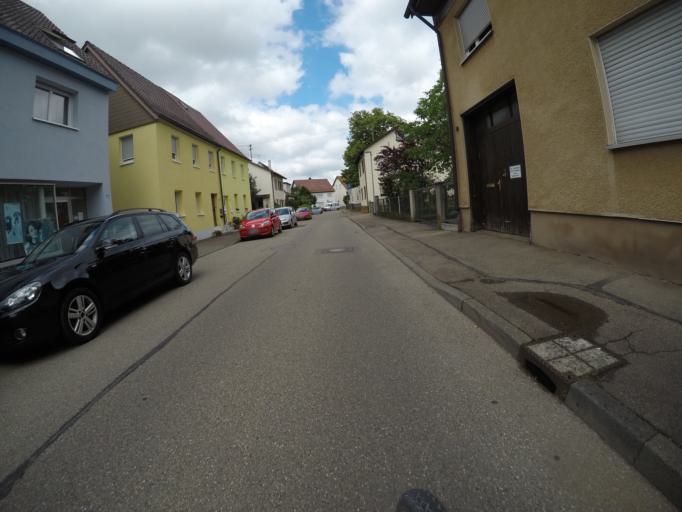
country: DE
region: Baden-Wuerttemberg
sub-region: Regierungsbezirk Stuttgart
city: Sussen
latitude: 48.6810
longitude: 9.7574
